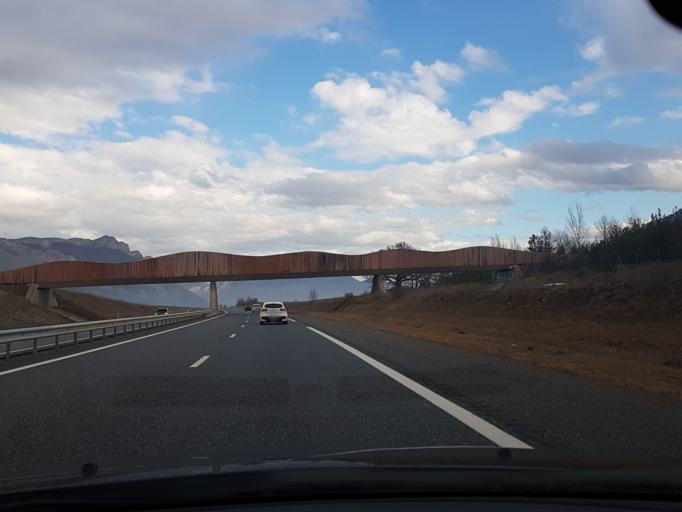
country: FR
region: Provence-Alpes-Cote d'Azur
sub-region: Departement des Hautes-Alpes
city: Laragne-Monteglin
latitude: 44.3539
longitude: 5.9145
